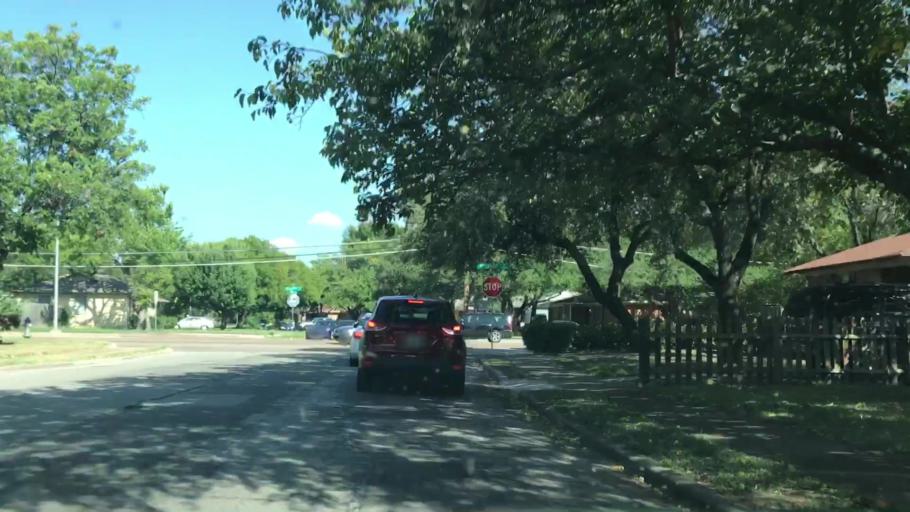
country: US
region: Texas
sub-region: Dallas County
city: Garland
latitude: 32.8332
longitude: -96.6748
